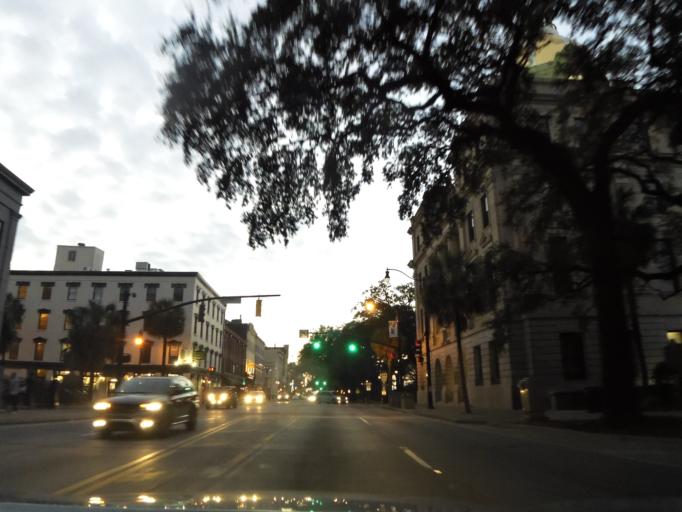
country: US
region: Georgia
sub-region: Chatham County
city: Savannah
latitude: 32.0808
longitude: -81.0907
